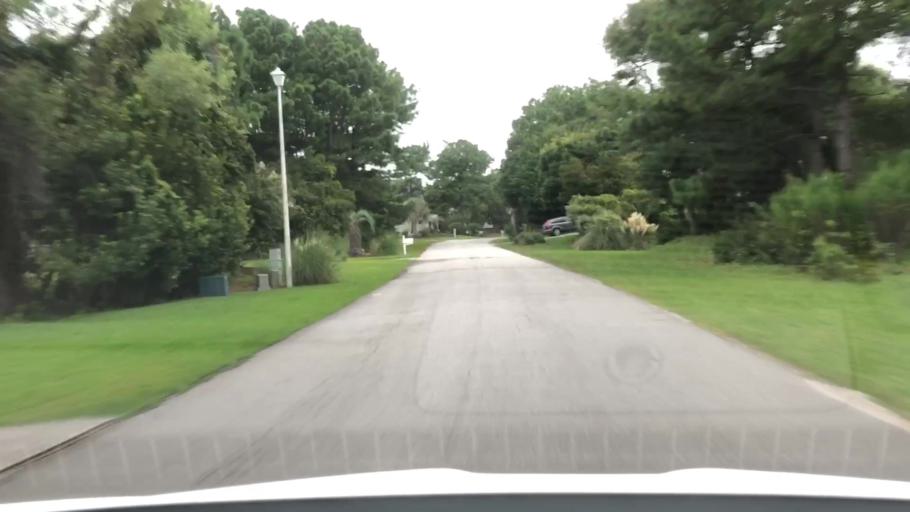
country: US
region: North Carolina
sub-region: Carteret County
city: Cedar Point
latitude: 34.6556
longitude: -77.0770
